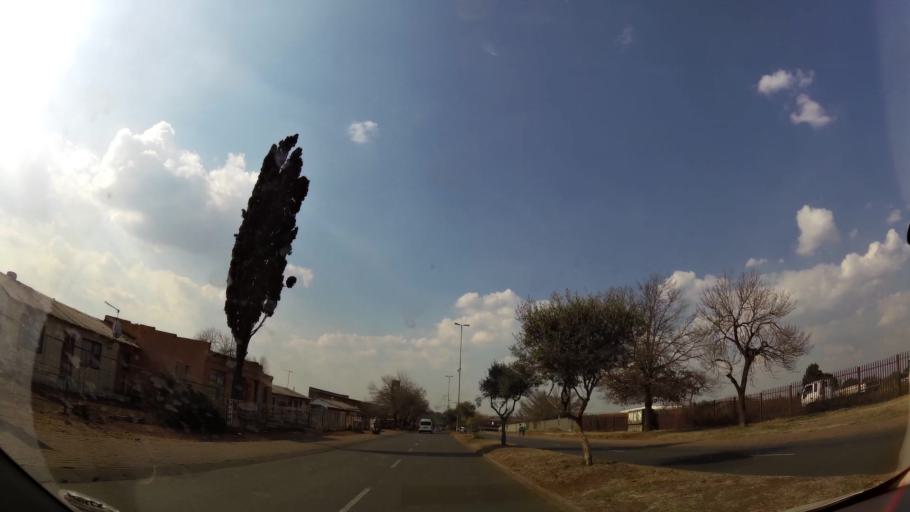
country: ZA
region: Gauteng
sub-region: Ekurhuleni Metropolitan Municipality
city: Germiston
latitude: -26.3130
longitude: 28.1535
